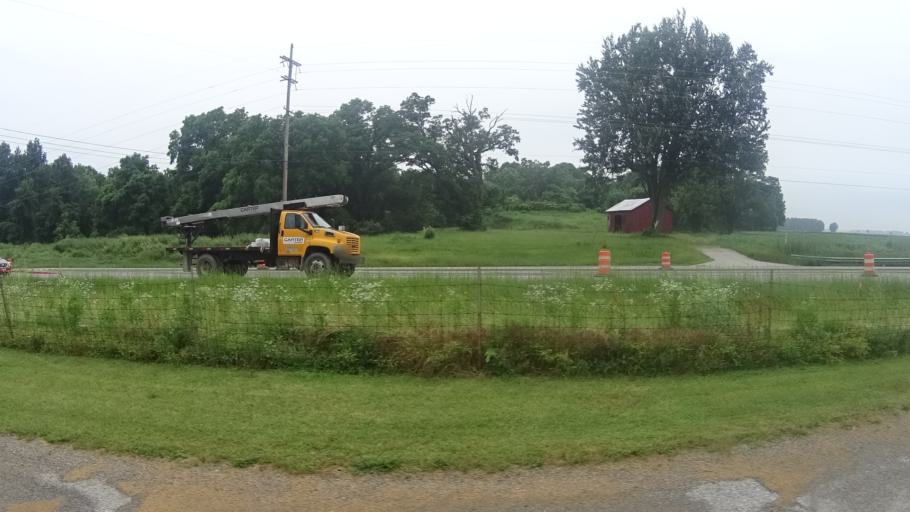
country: US
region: Ohio
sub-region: Erie County
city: Milan
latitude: 41.3108
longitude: -82.6062
